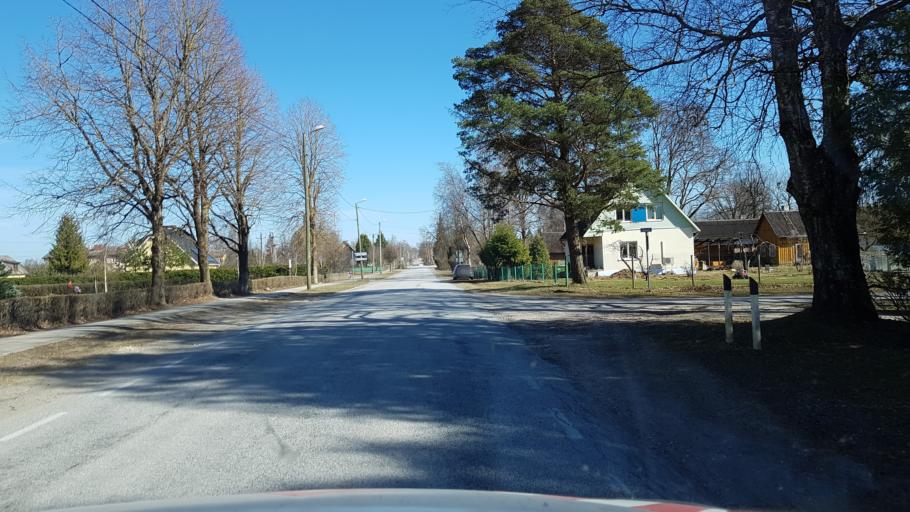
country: EE
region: Laeaene-Virumaa
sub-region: Rakke vald
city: Rakke
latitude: 58.9913
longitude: 26.2306
